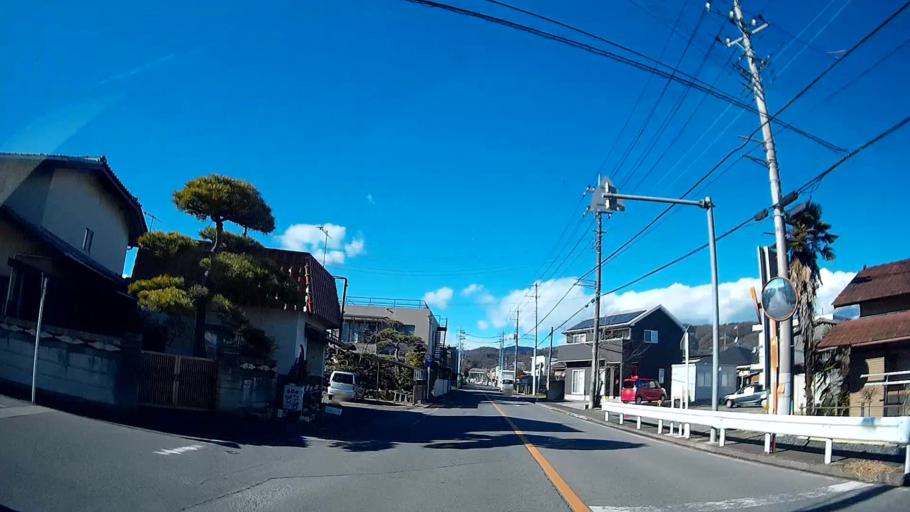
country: JP
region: Saitama
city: Yorii
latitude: 36.1156
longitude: 139.1895
